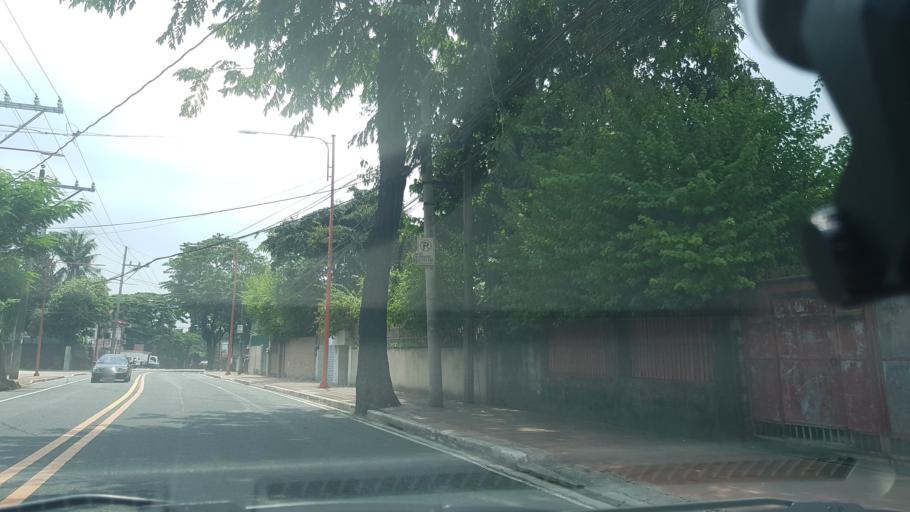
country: PH
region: Calabarzon
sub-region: Province of Rizal
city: Antipolo
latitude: 14.6540
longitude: 121.1138
